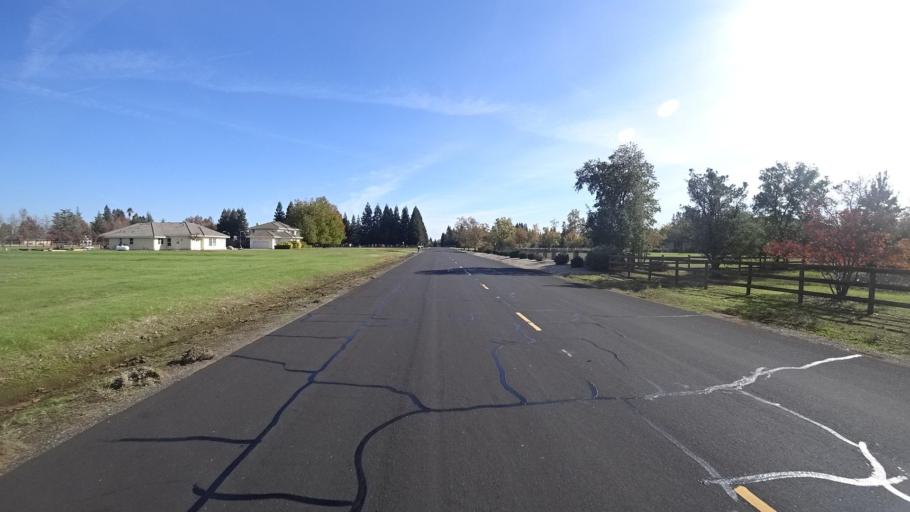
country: US
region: California
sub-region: Sacramento County
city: Wilton
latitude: 38.4346
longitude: -121.2878
